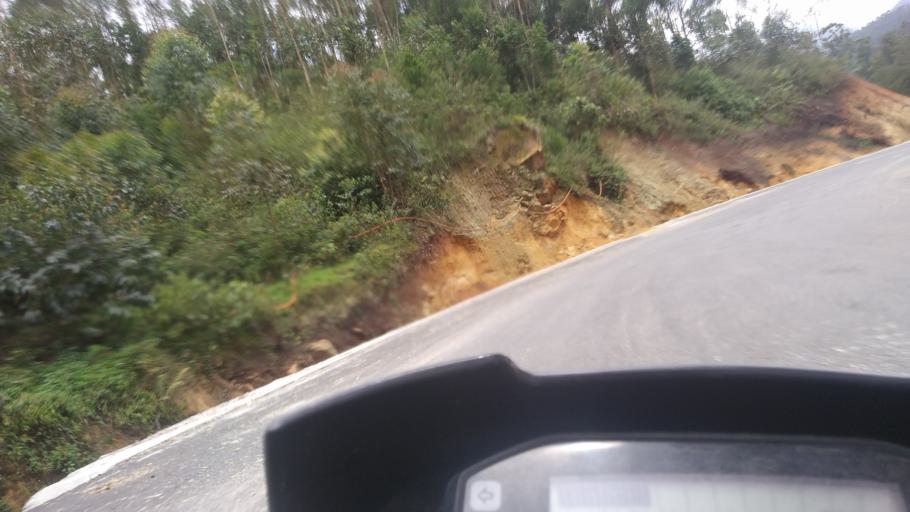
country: IN
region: Kerala
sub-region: Idukki
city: Munnar
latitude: 10.0740
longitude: 77.0910
